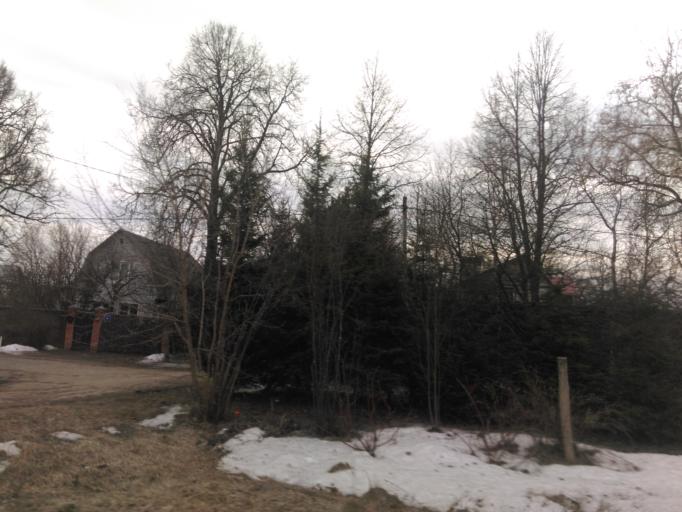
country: RU
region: Moskovskaya
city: Zvenigorod
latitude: 55.7352
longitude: 36.9344
